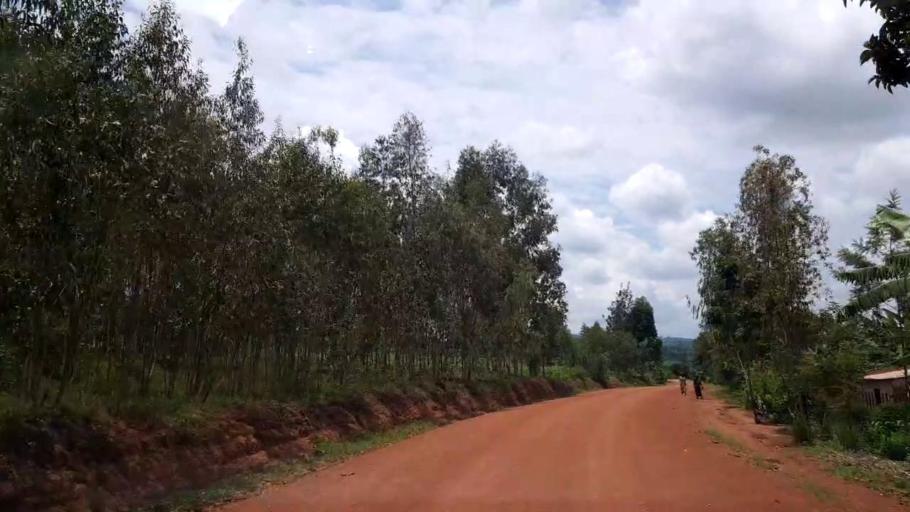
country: RW
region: Northern Province
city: Byumba
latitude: -1.5723
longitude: 30.3024
